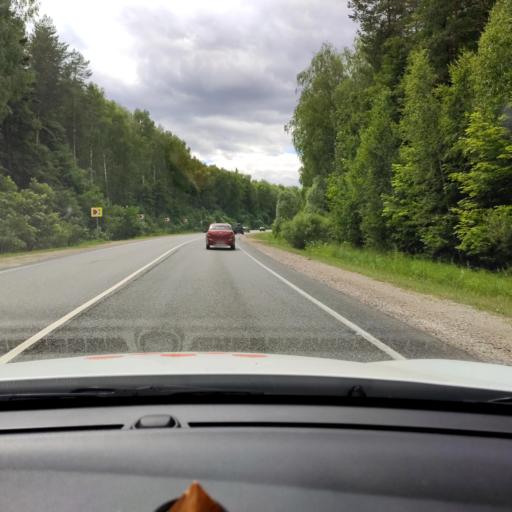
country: RU
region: Tatarstan
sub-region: Zelenodol'skiy Rayon
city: Zelenodolsk
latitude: 55.8827
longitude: 48.5118
